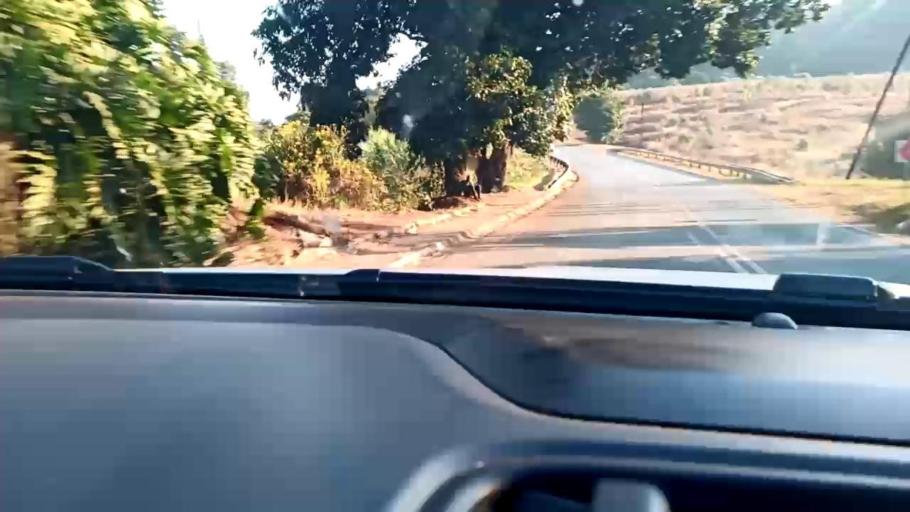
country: ZA
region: Limpopo
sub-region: Mopani District Municipality
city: Duiwelskloof
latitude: -23.6986
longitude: 30.1373
